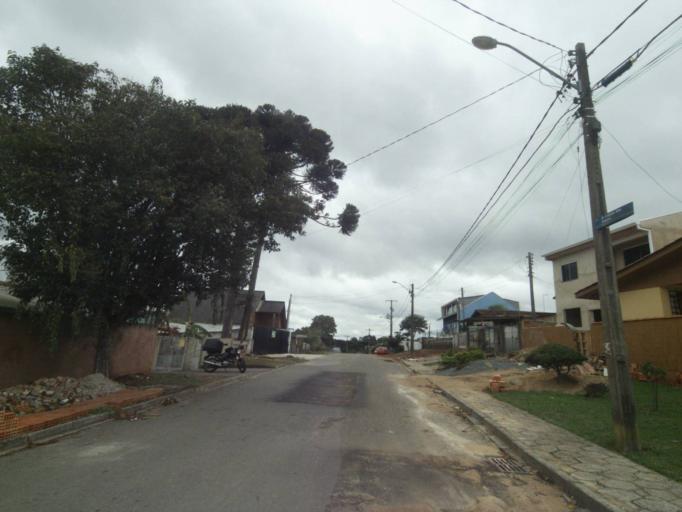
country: BR
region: Parana
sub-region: Sao Jose Dos Pinhais
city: Sao Jose dos Pinhais
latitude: -25.5407
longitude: -49.2976
